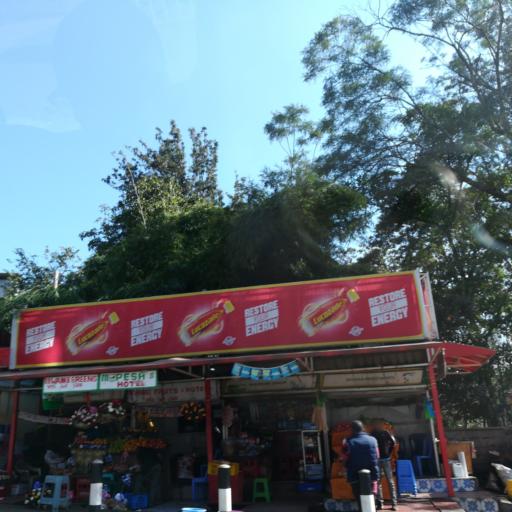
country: KE
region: Nairobi Area
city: Nairobi
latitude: -1.2951
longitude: 36.8061
